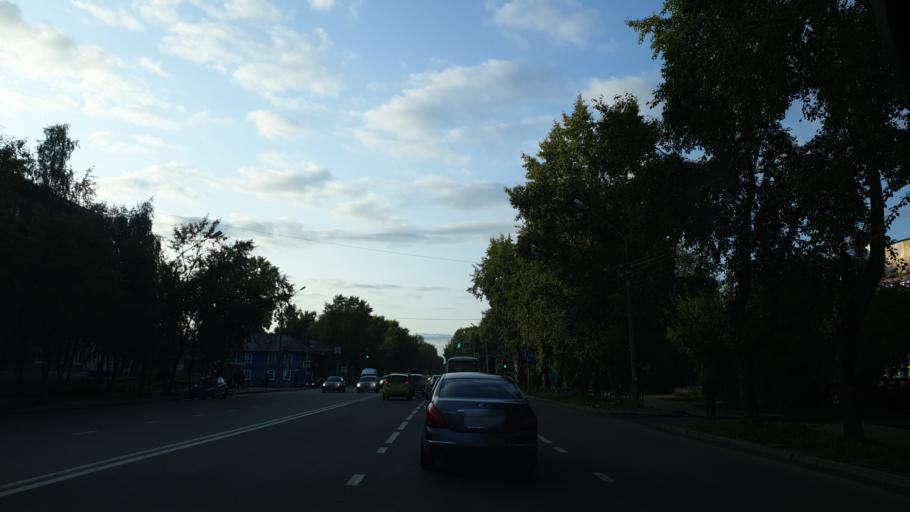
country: RU
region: Komi Republic
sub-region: Syktyvdinskiy Rayon
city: Syktyvkar
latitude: 61.6682
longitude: 50.8121
